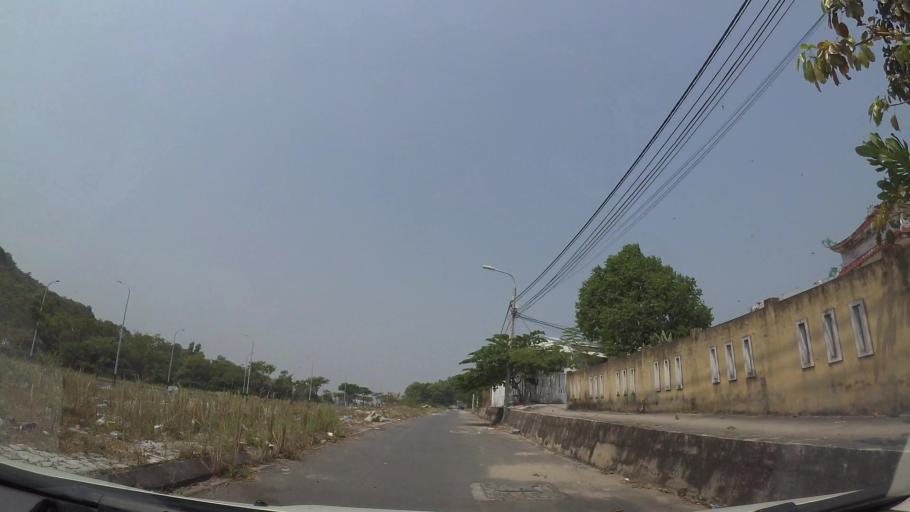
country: VN
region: Da Nang
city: Ngu Hanh Son
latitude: 16.0063
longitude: 108.2566
